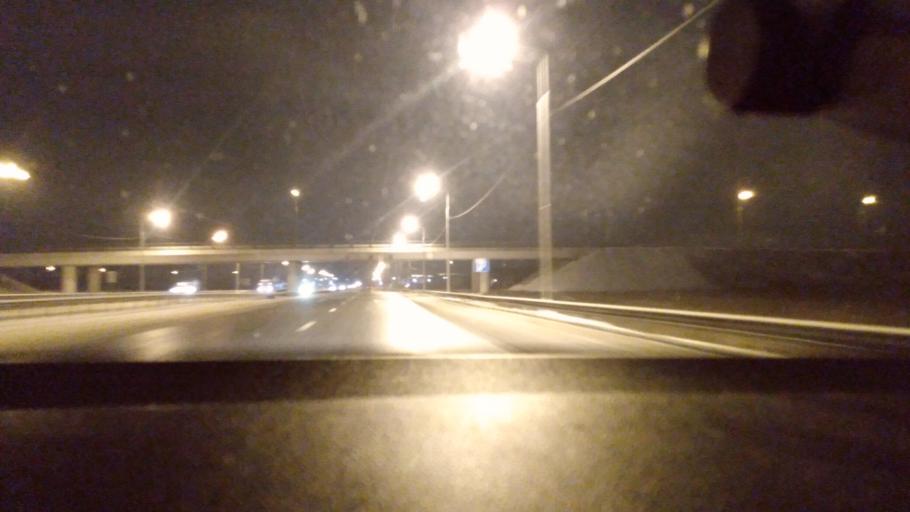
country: RU
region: Moskovskaya
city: Kolomna
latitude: 55.1207
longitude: 38.8205
